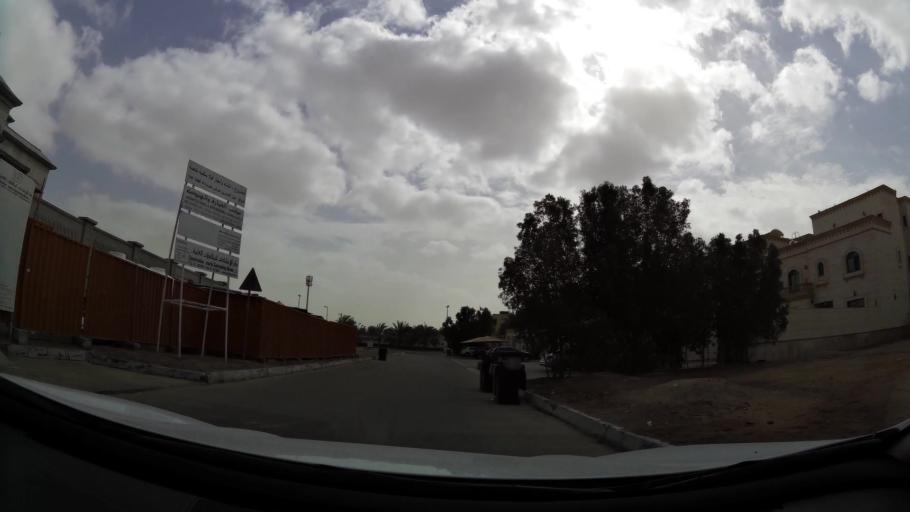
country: AE
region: Abu Dhabi
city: Abu Dhabi
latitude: 24.4136
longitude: 54.4968
